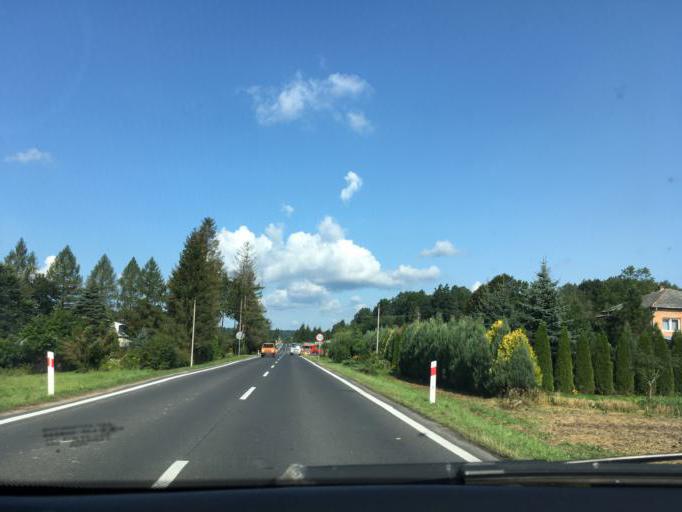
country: PL
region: Subcarpathian Voivodeship
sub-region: Powiat leski
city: Olszanica
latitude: 49.4683
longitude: 22.4628
